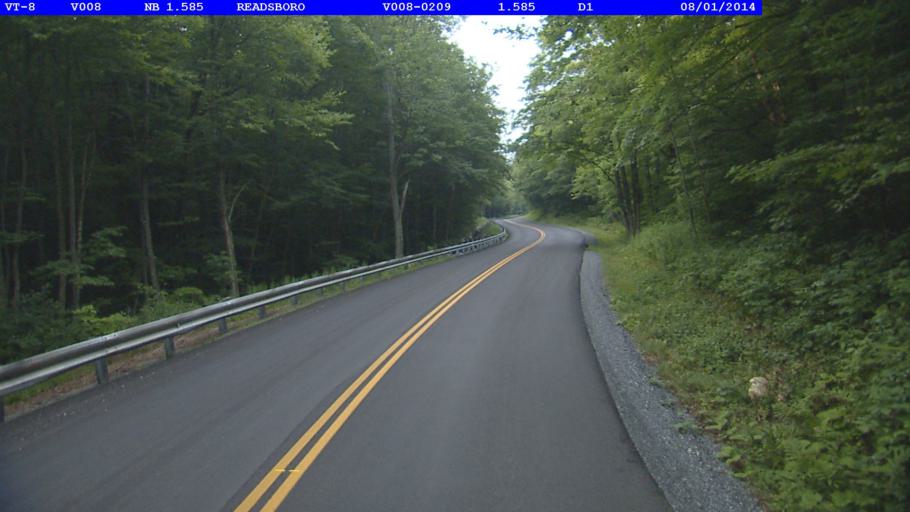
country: US
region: Massachusetts
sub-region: Berkshire County
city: North Adams
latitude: 42.8488
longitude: -72.9884
